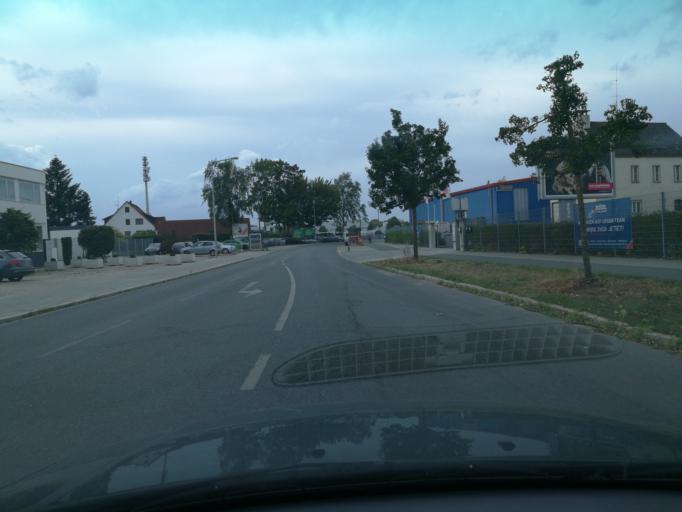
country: DE
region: Bavaria
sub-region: Regierungsbezirk Mittelfranken
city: Wetzendorf
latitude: 49.4694
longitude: 11.0447
